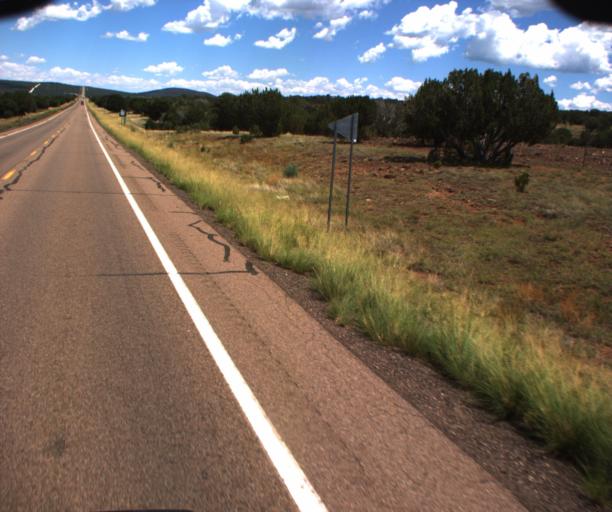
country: US
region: Arizona
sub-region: Navajo County
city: White Mountain Lake
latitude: 34.2801
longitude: -109.8706
